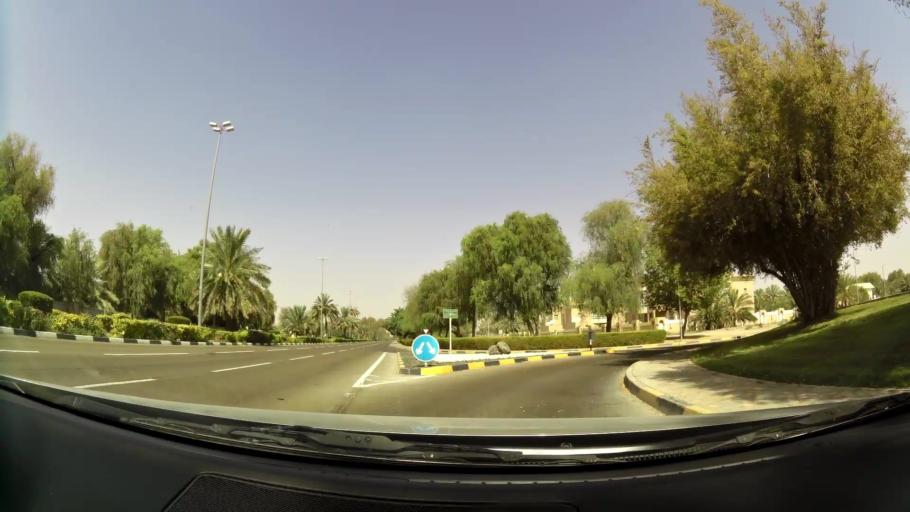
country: OM
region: Al Buraimi
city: Al Buraymi
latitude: 24.2977
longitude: 55.7809
